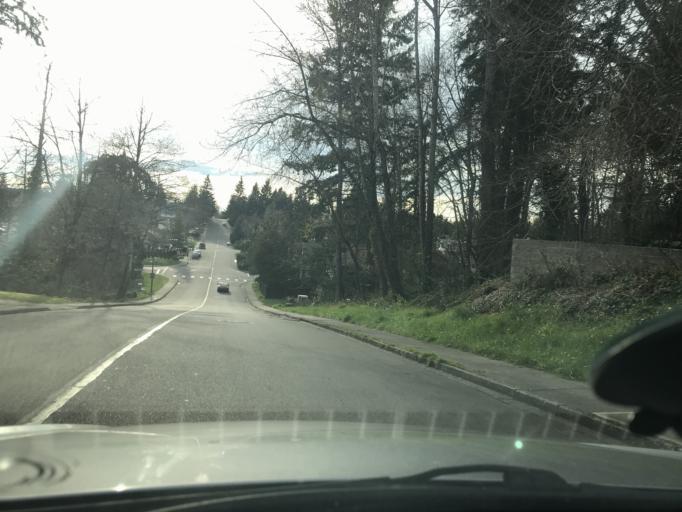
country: US
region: Washington
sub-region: King County
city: East Hill-Meridian
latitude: 47.4086
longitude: -122.1744
